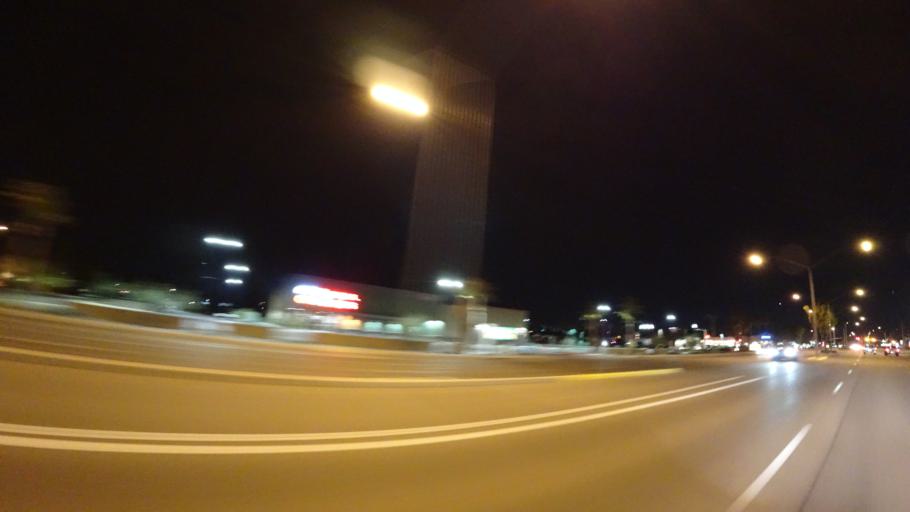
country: US
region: Arizona
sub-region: Maricopa County
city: Gilbert
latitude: 33.3791
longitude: -111.7849
